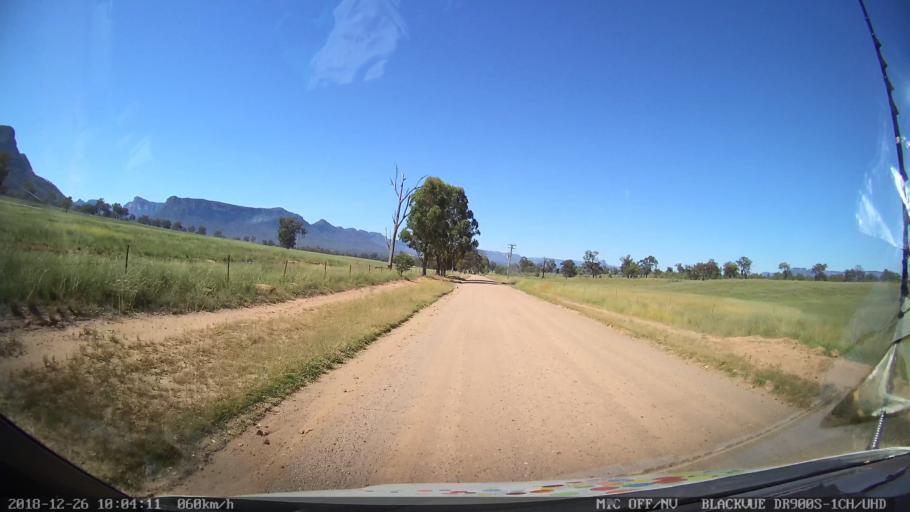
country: AU
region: New South Wales
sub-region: Mid-Western Regional
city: Kandos
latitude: -33.0680
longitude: 150.2154
